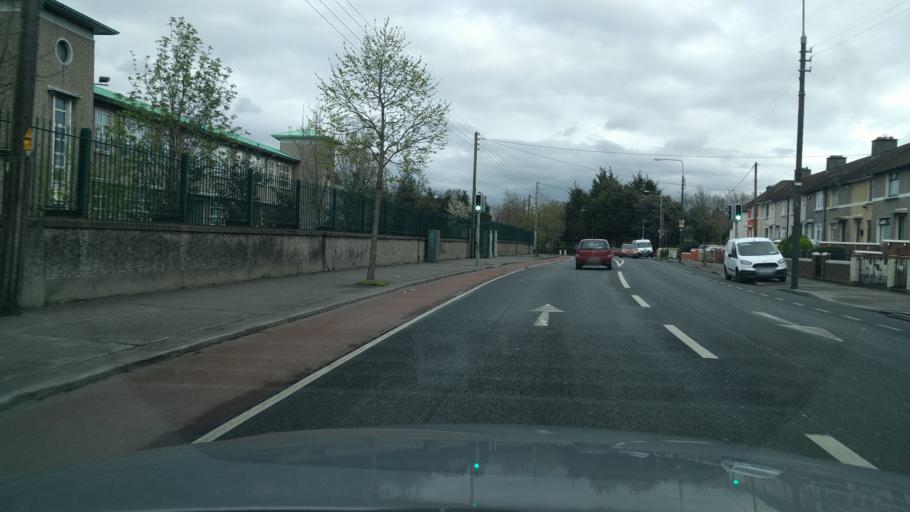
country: IE
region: Leinster
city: Chapelizod
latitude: 53.3424
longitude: -6.3443
